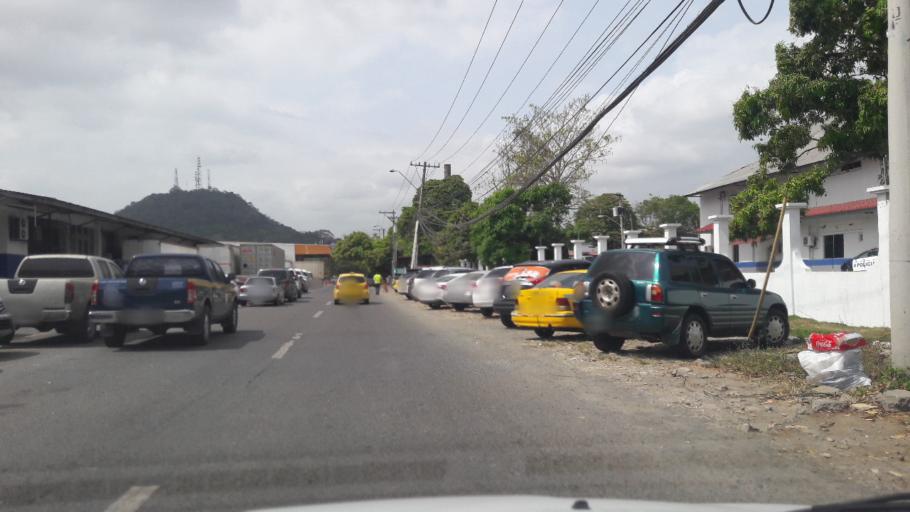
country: PA
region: Panama
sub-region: Distrito de Panama
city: Ancon
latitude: 8.9736
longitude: -79.5472
